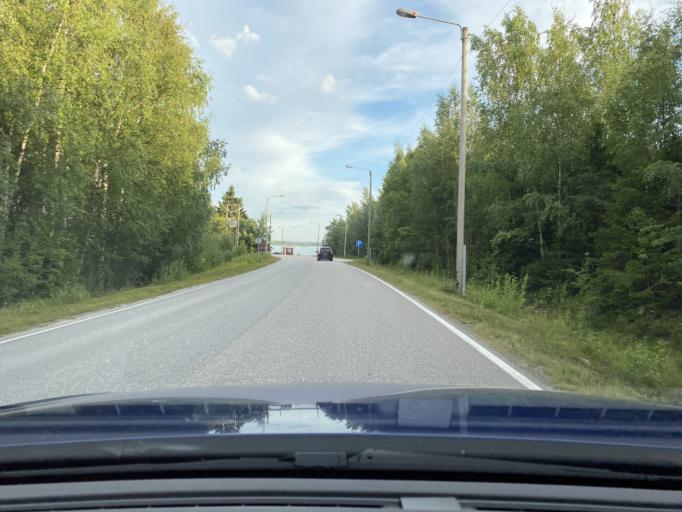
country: FI
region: Ostrobothnia
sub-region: Vaasa
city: Korsnaes
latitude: 62.9457
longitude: 21.1757
